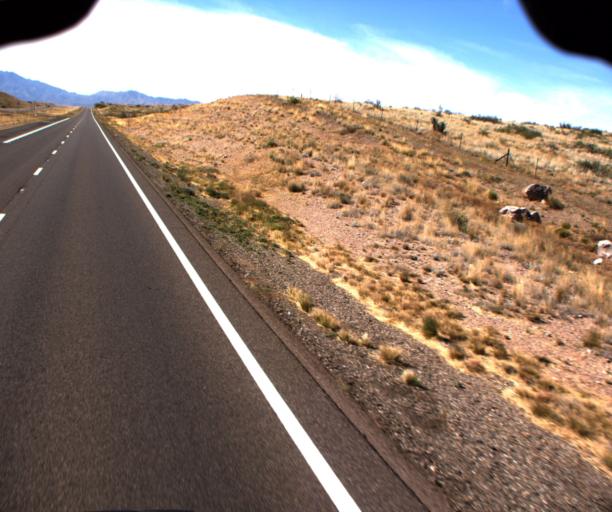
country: US
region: Arizona
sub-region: Cochise County
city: Willcox
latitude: 32.4196
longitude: -109.6628
